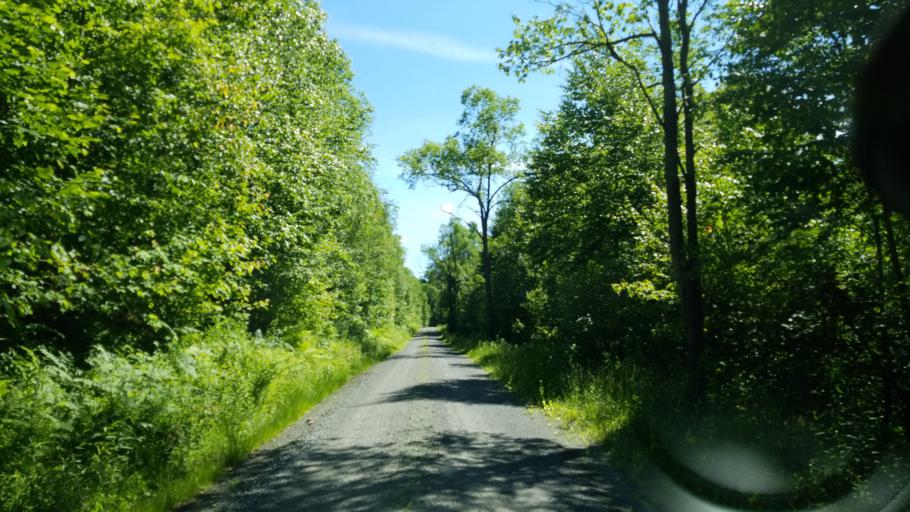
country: US
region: Pennsylvania
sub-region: Clearfield County
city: Clearfield
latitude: 41.2118
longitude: -78.3864
